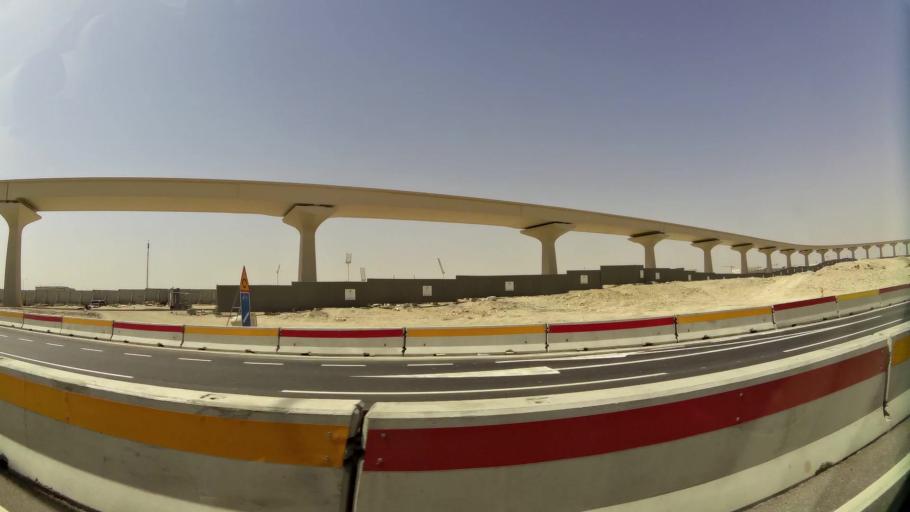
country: QA
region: Baladiyat Umm Salal
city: Umm Salal Muhammad
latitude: 25.3790
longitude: 51.4989
